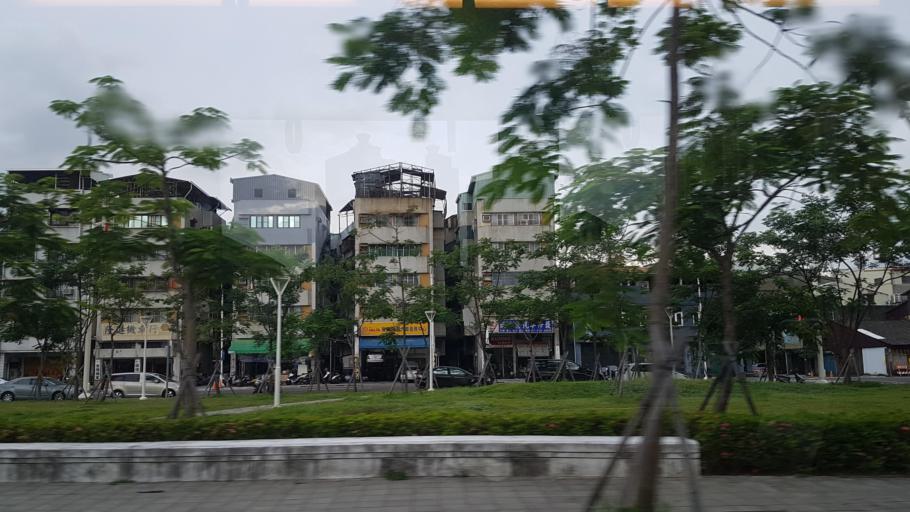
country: TW
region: Kaohsiung
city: Kaohsiung
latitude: 22.6484
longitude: 120.2815
